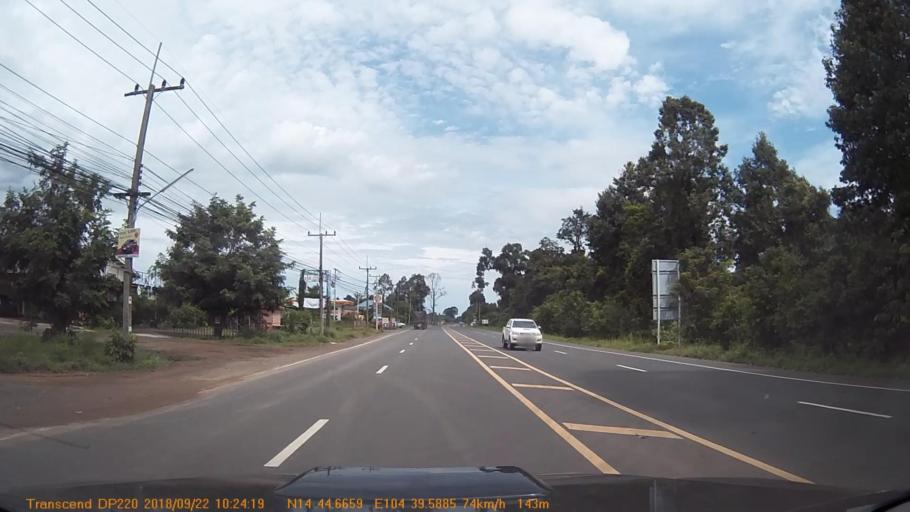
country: TH
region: Sisaket
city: Benchalak
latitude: 14.7447
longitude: 104.6597
